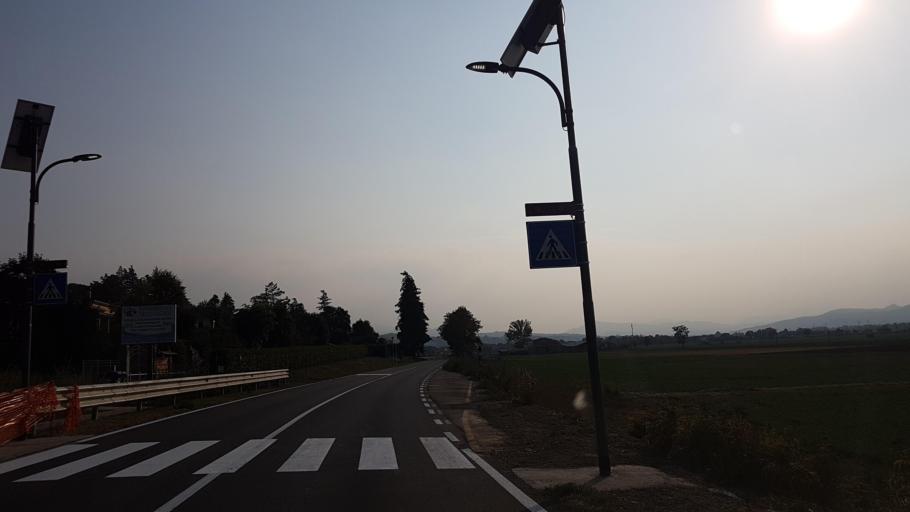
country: IT
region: Emilia-Romagna
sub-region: Provincia di Parma
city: Gaiano
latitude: 44.7334
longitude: 10.1861
